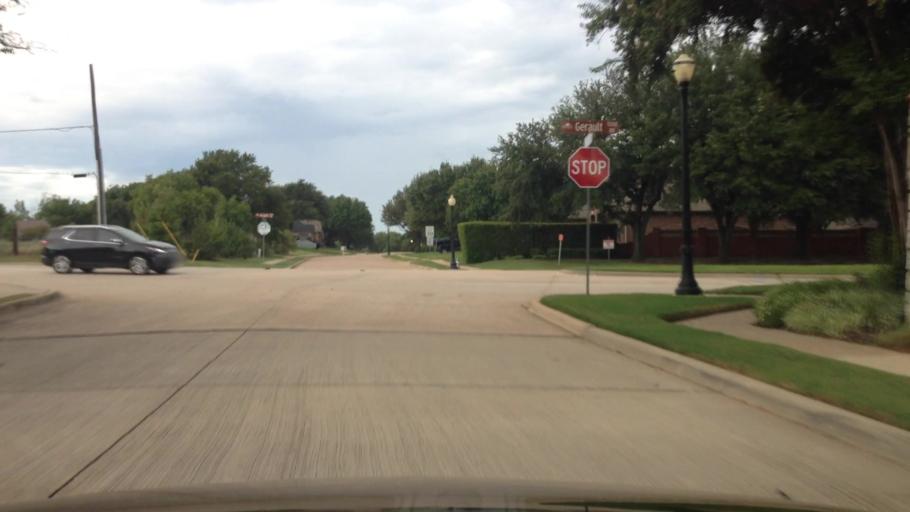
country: US
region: Texas
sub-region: Denton County
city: Flower Mound
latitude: 33.0029
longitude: -97.0447
